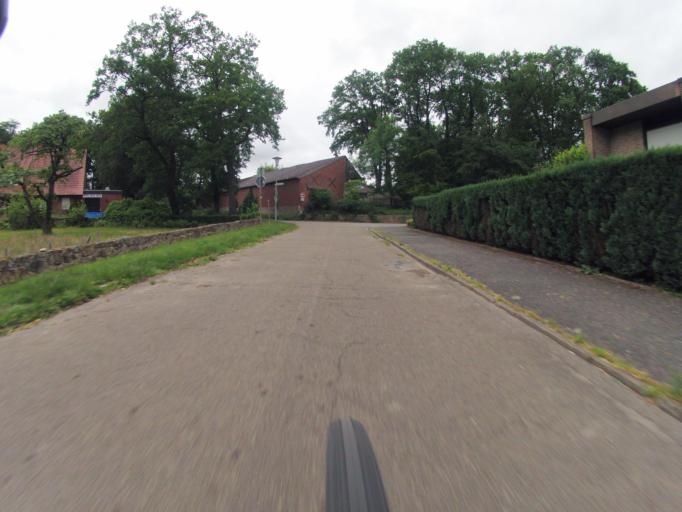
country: DE
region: North Rhine-Westphalia
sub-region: Regierungsbezirk Munster
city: Dreierwalde
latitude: 52.2404
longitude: 7.5207
